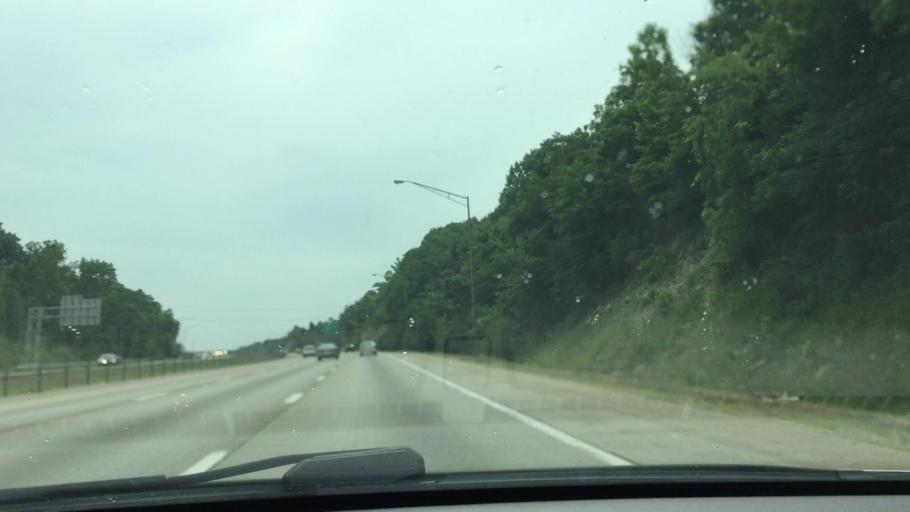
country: US
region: Kentucky
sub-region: Kenton County
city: Fort Wright
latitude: 39.0241
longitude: -84.5228
